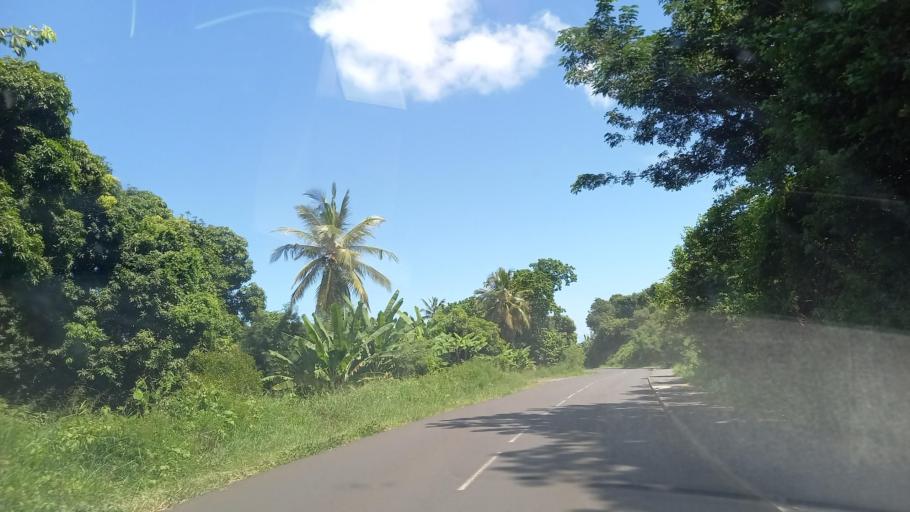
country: YT
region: Boueni
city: Boueni
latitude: -12.9241
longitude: 45.0961
